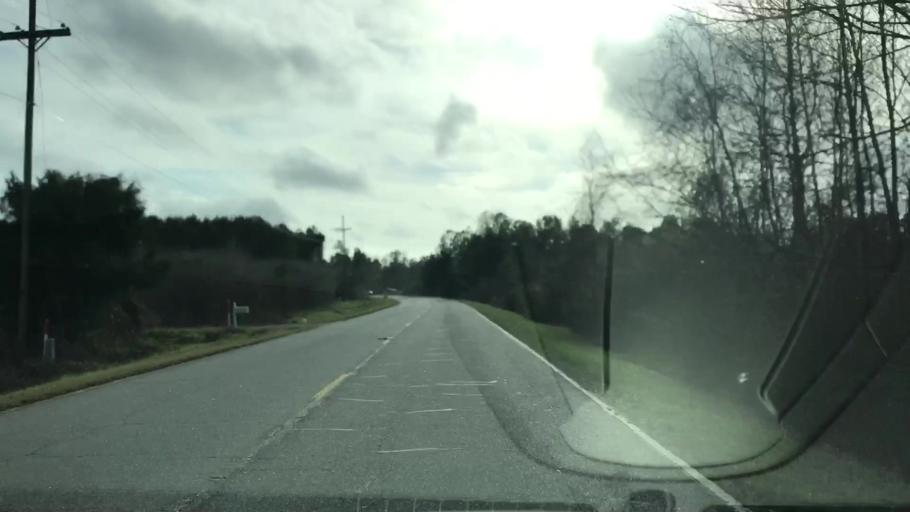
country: US
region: South Carolina
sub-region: Williamsburg County
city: Andrews
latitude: 33.3513
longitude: -79.6604
